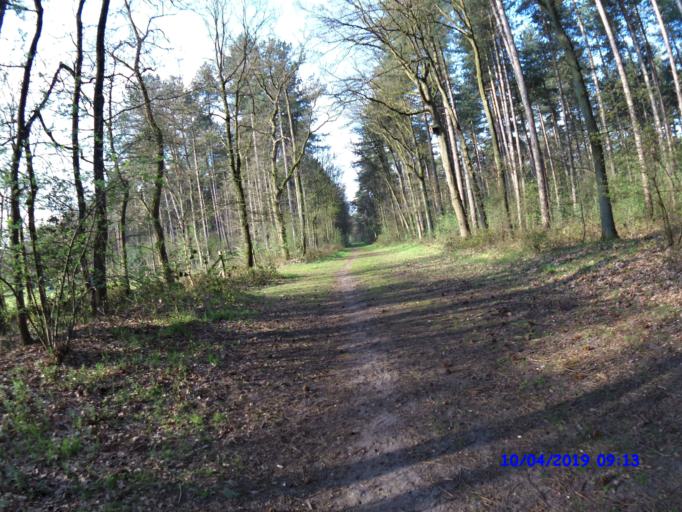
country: BE
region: Flanders
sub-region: Provincie Limburg
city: Leopoldsburg
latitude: 51.1049
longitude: 5.2456
